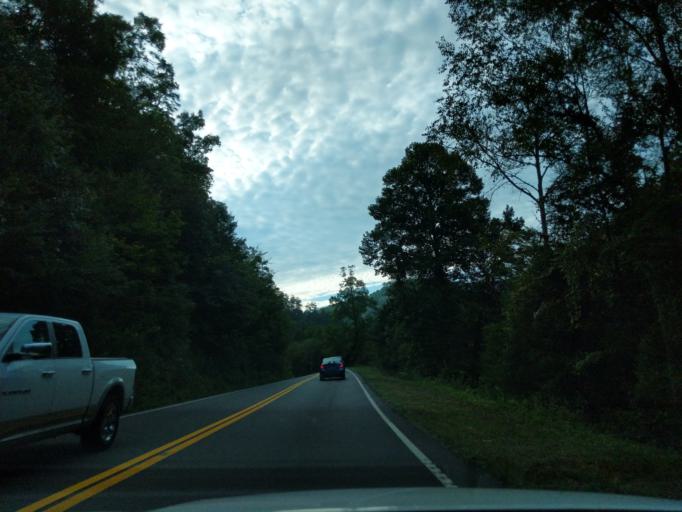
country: US
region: Tennessee
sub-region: Polk County
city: Benton
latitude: 35.0991
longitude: -84.5521
